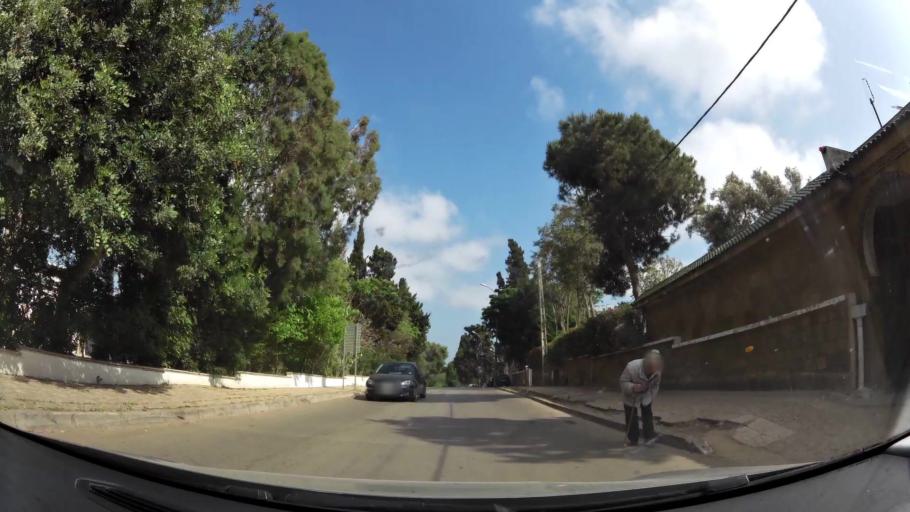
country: MA
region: Rabat-Sale-Zemmour-Zaer
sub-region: Rabat
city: Rabat
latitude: 33.9741
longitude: -6.8622
